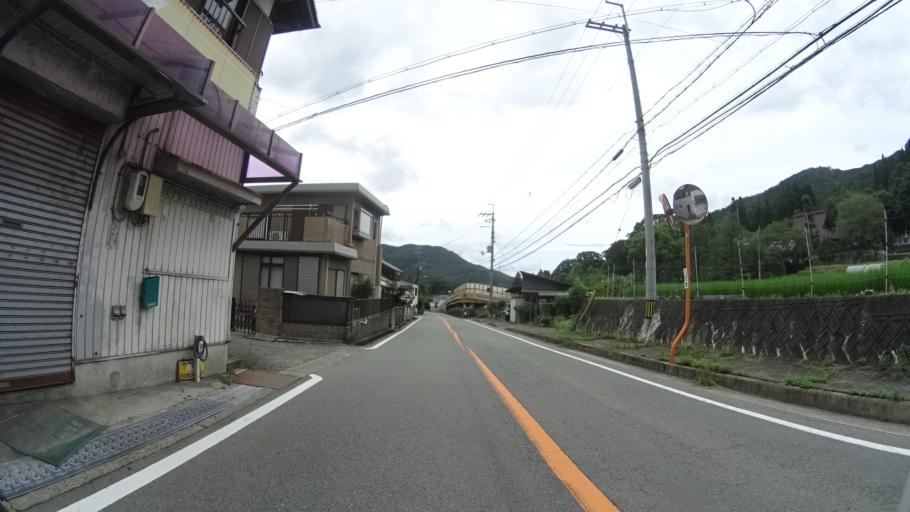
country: JP
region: Kyoto
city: Kameoka
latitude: 34.9711
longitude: 135.4654
